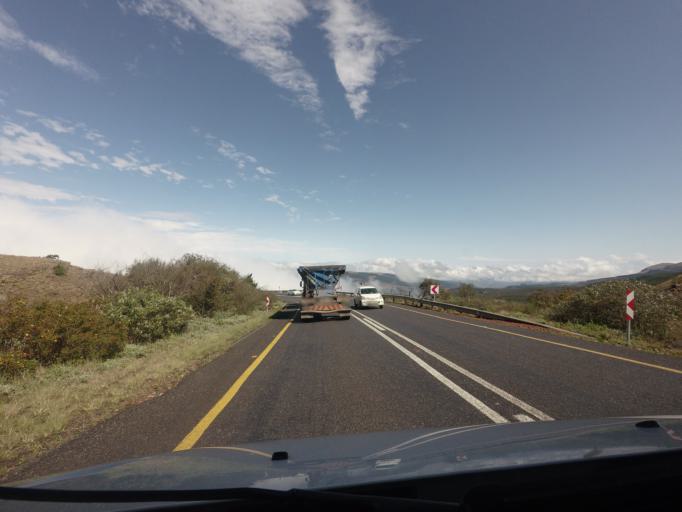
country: ZA
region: Mpumalanga
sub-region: Ehlanzeni District
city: Lydenburg
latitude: -25.1581
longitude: 30.6260
